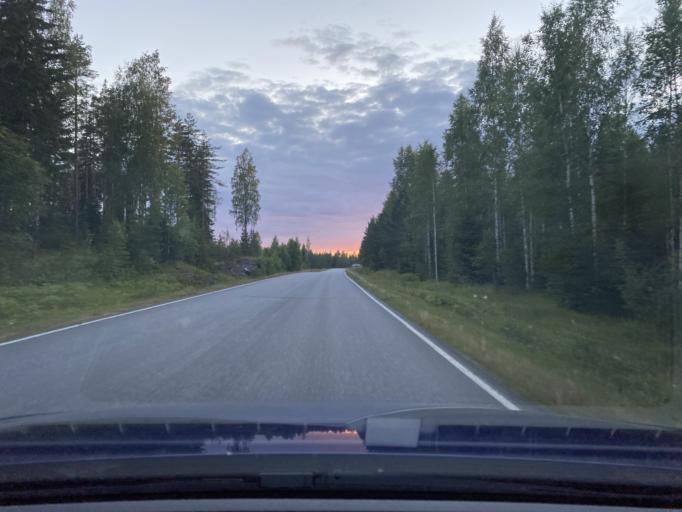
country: FI
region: Haeme
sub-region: Forssa
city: Tammela
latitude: 60.9139
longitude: 23.8464
